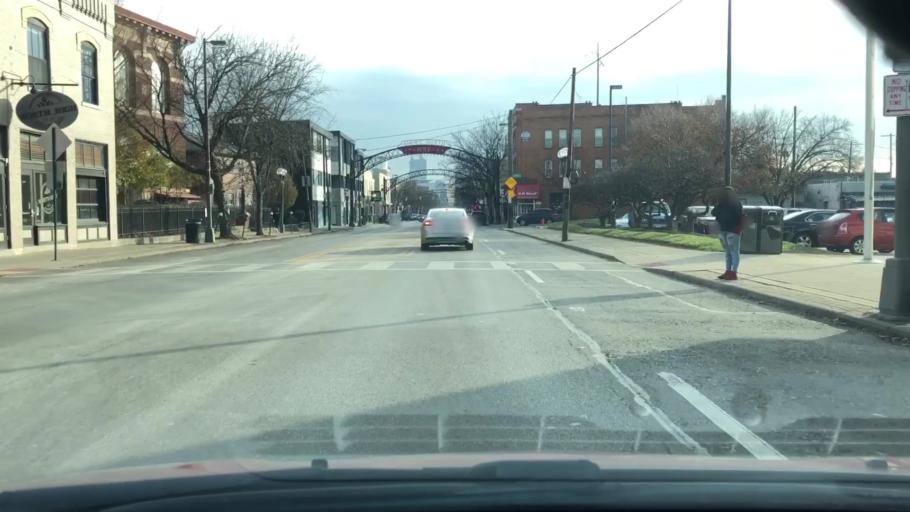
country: US
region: Ohio
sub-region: Franklin County
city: Columbus
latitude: 39.9888
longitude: -83.0059
